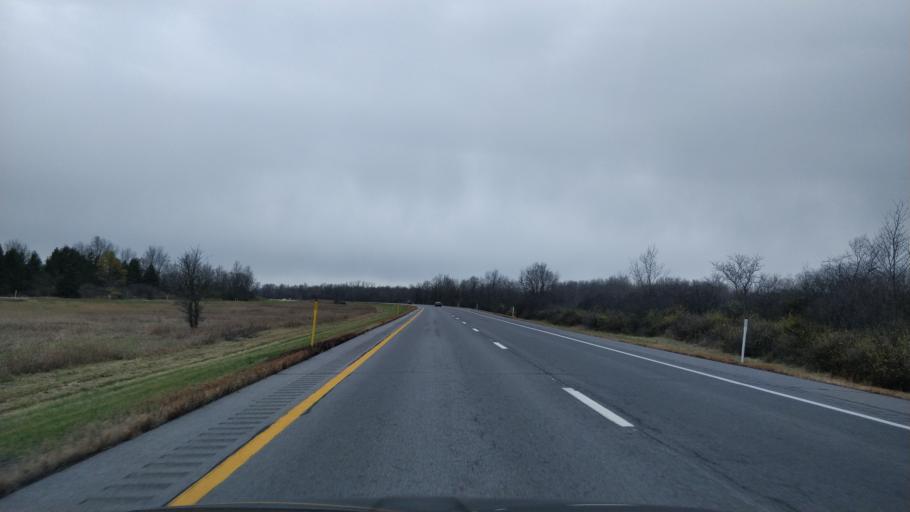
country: US
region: New York
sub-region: Jefferson County
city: Calcium
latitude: 44.1014
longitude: -75.9062
